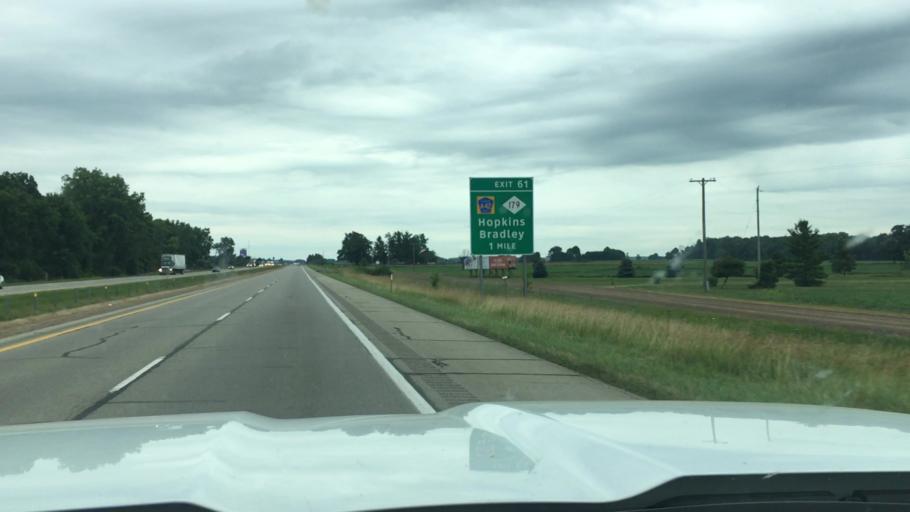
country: US
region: Michigan
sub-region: Allegan County
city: Wayland
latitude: 42.6479
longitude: -85.6623
